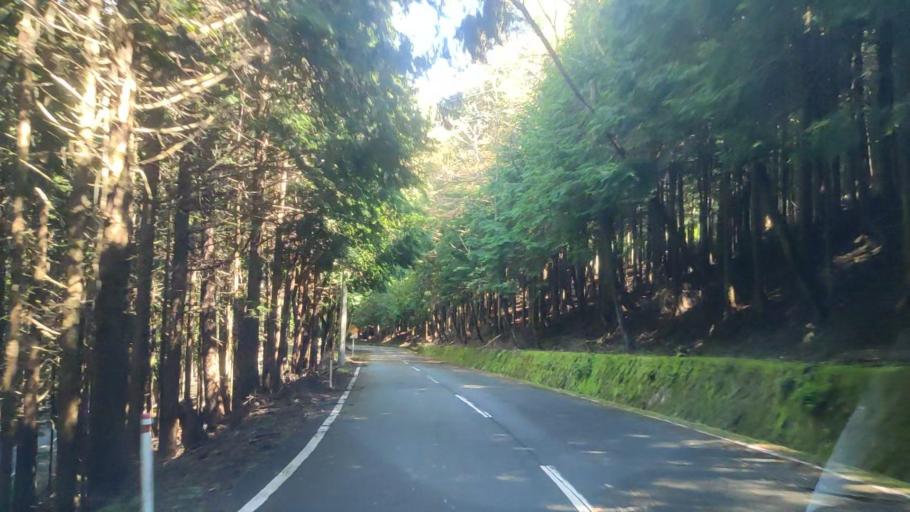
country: JP
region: Yamanashi
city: Fujikawaguchiko
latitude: 35.5692
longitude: 138.7754
